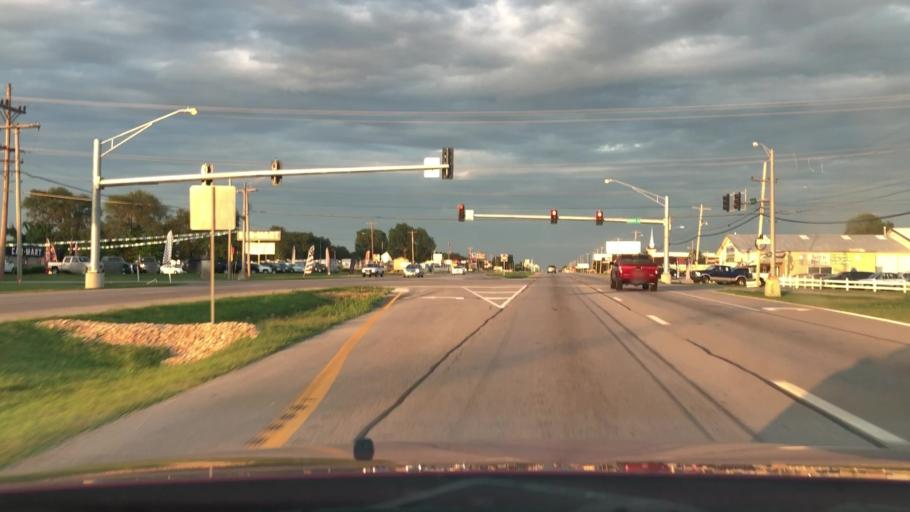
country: US
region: Missouri
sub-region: Greene County
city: Springfield
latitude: 37.1829
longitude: -93.3460
